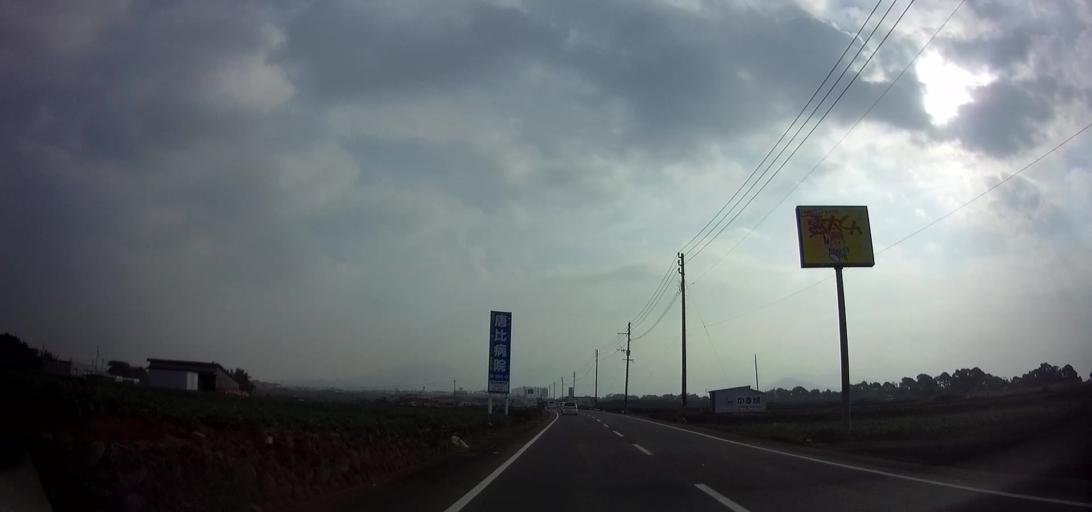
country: JP
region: Nagasaki
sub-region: Isahaya-shi
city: Isahaya
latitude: 32.7971
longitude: 130.1539
